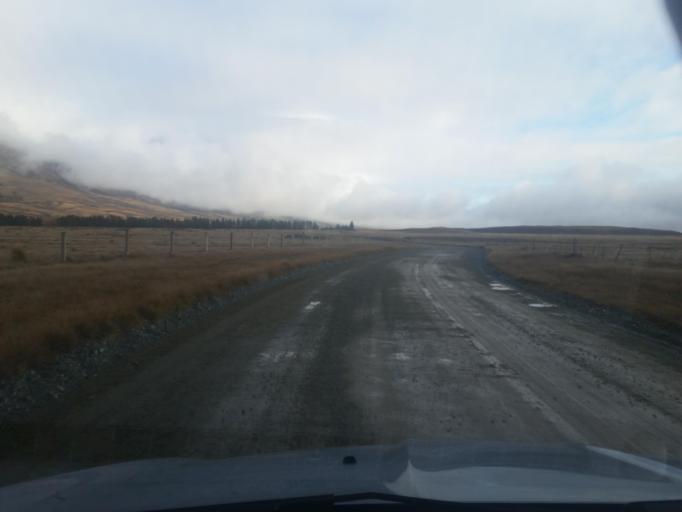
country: NZ
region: Canterbury
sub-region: Ashburton District
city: Methven
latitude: -43.6156
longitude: 171.0754
